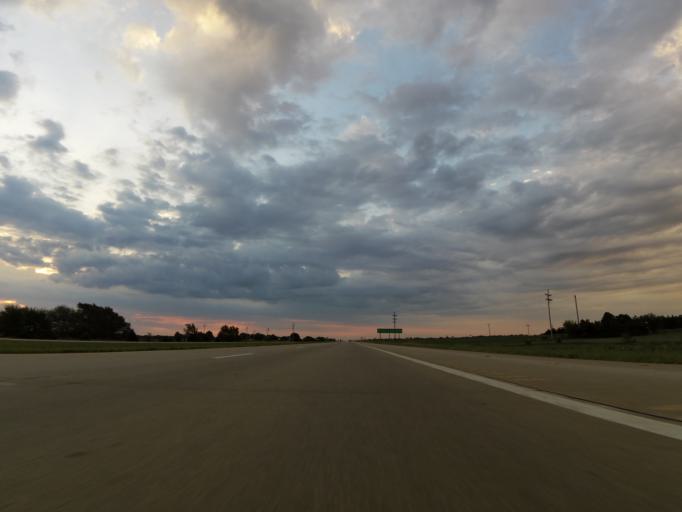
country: US
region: Kansas
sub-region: Reno County
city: South Hutchinson
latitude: 37.9565
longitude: -97.9055
